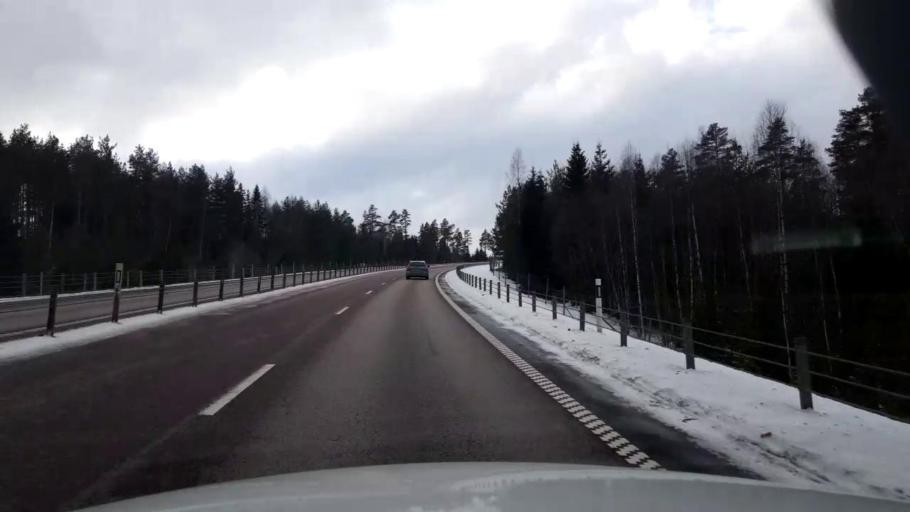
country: SE
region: Gaevleborg
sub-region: Hudiksvalls Kommun
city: Hudiksvall
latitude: 61.7960
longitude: 17.1678
